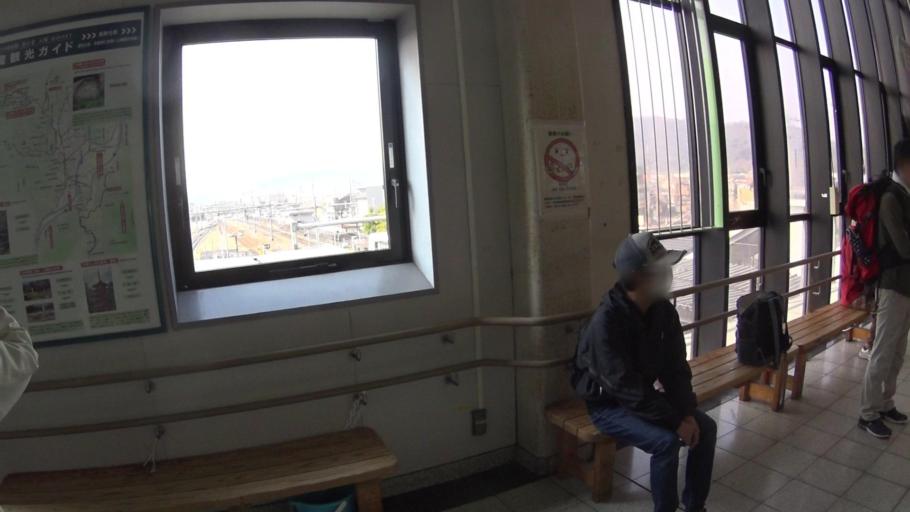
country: JP
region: Nara
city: Nara-shi
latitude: 34.7418
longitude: 135.8692
